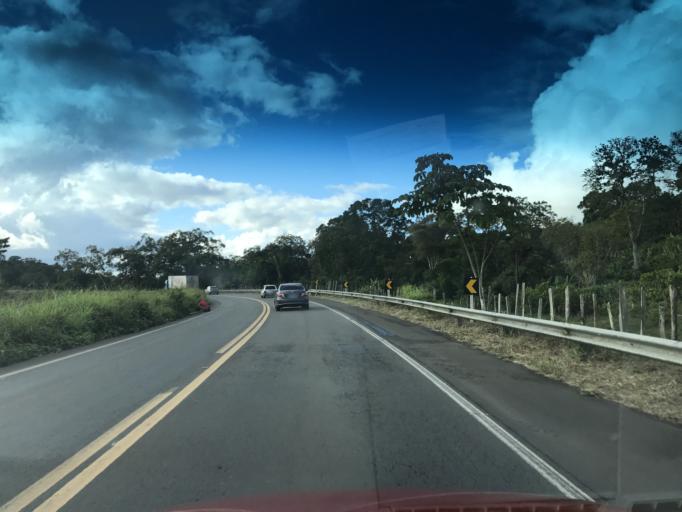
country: BR
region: Bahia
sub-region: Ibirapitanga
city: Ibirapitanga
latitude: -14.1565
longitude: -39.3268
